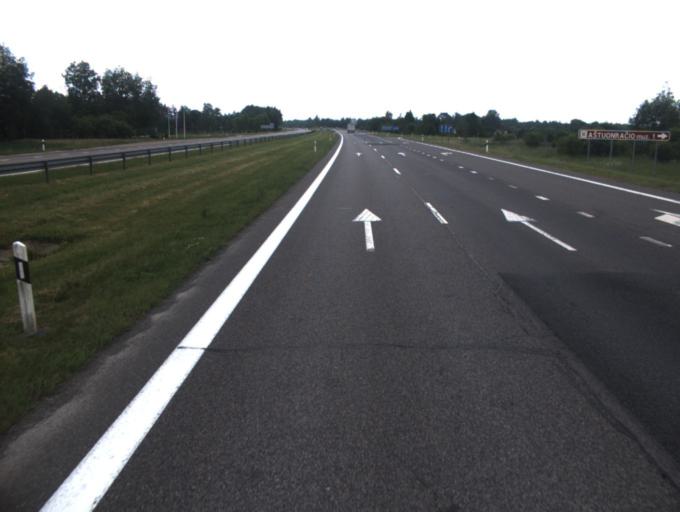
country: LT
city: Skaudvile
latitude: 55.4252
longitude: 22.7615
